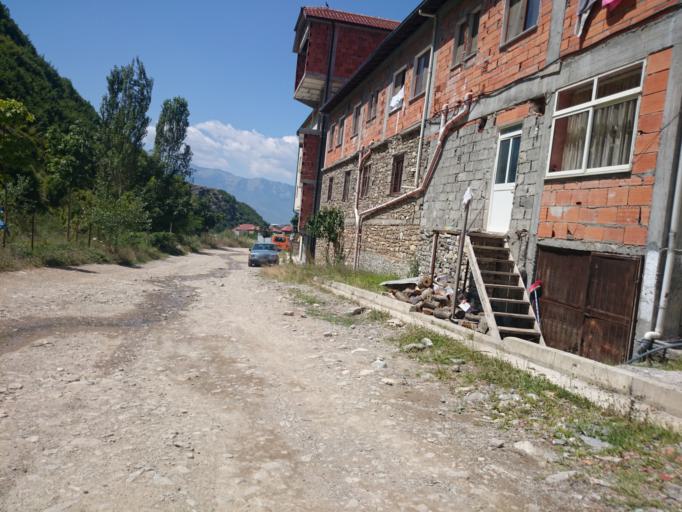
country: AL
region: Diber
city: Peshkopi
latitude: 41.6853
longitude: 20.4500
